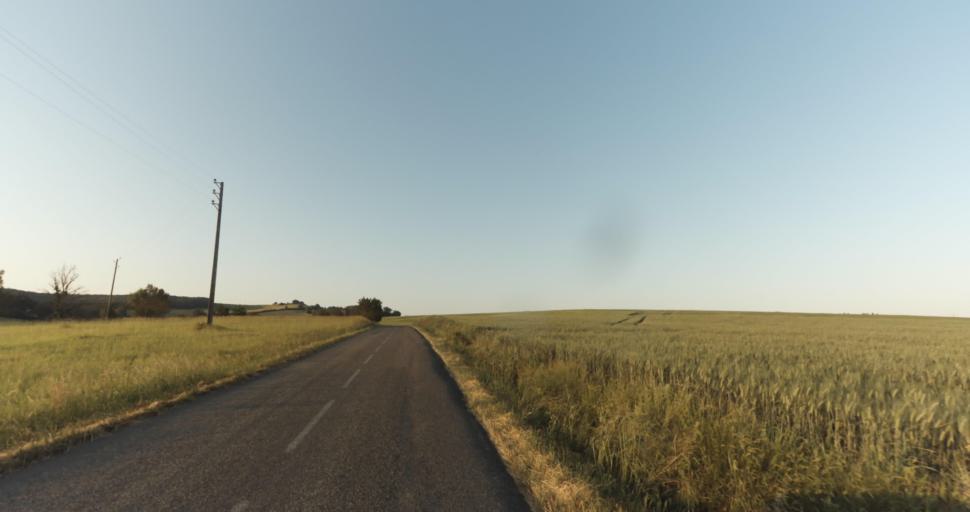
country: FR
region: Midi-Pyrenees
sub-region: Departement du Gers
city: Pujaudran
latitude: 43.6221
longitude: 1.1558
